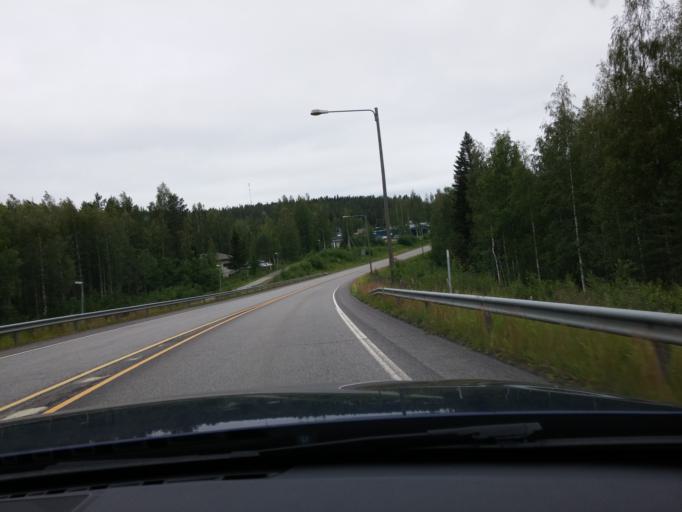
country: FI
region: Central Finland
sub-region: Saarijaervi-Viitasaari
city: Saarijaervi
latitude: 62.6872
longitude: 25.3149
